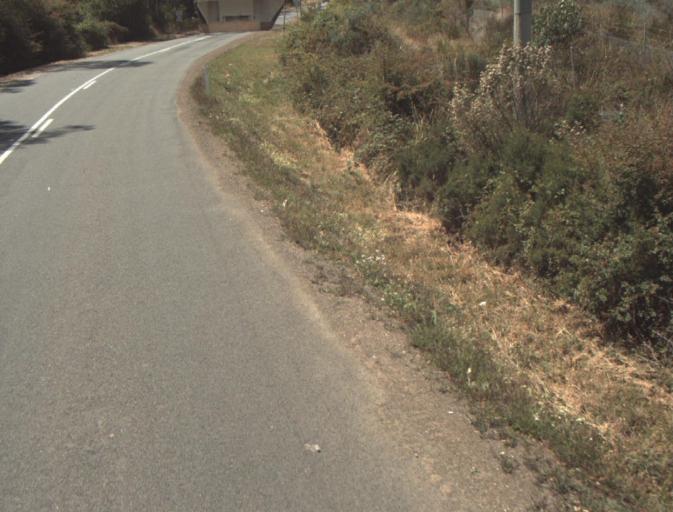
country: AU
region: Tasmania
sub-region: Launceston
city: Mayfield
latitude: -41.3669
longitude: 147.1419
